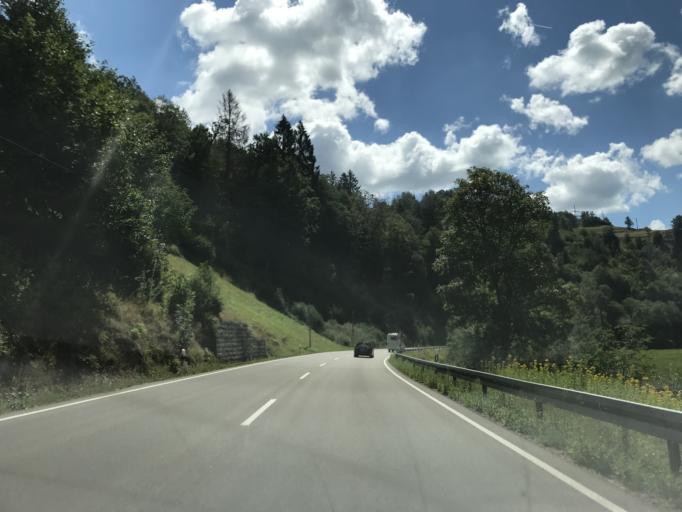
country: DE
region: Baden-Wuerttemberg
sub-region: Freiburg Region
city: Wembach
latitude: 47.7385
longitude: 7.8832
